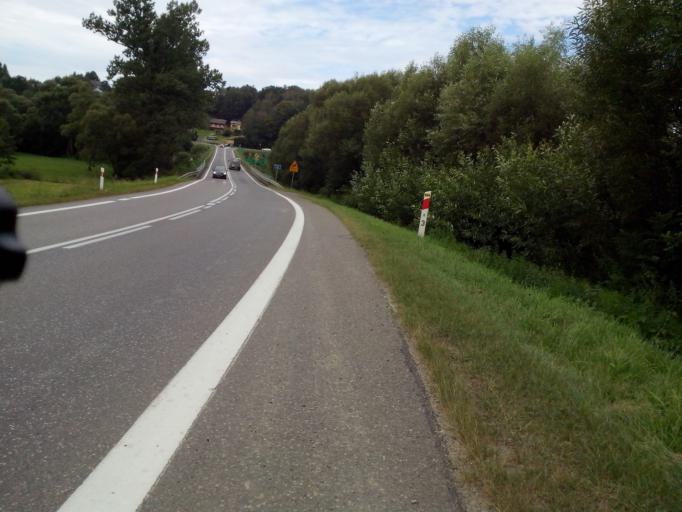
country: PL
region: Subcarpathian Voivodeship
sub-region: Powiat brzozowski
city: Domaradz
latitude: 49.7735
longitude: 21.9483
